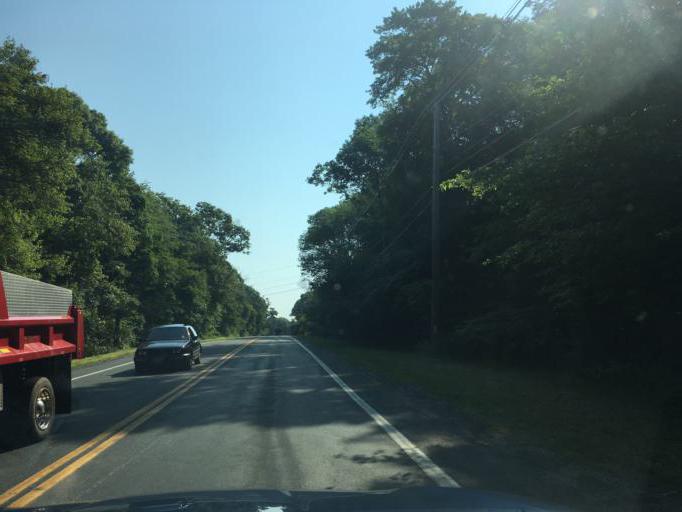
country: US
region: Rhode Island
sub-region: Washington County
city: Kingston
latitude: 41.4835
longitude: -71.5003
